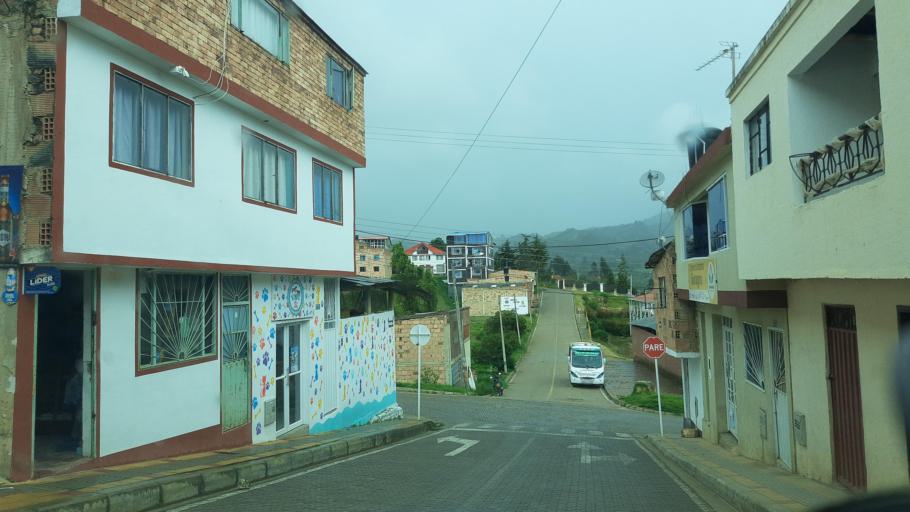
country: CO
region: Boyaca
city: Turmeque
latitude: 5.3546
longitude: -73.4562
